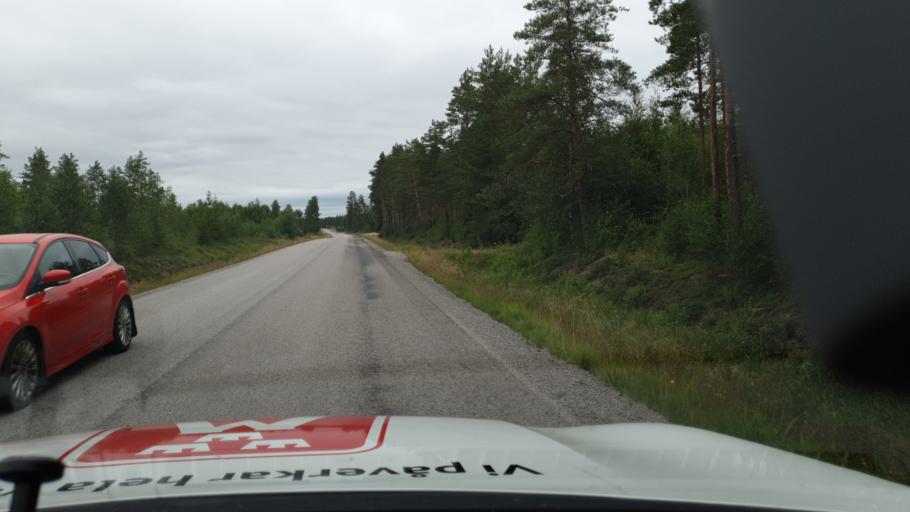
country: SE
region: Vaesterbotten
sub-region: Umea Kommun
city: Ersmark
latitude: 63.9060
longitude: 20.3132
